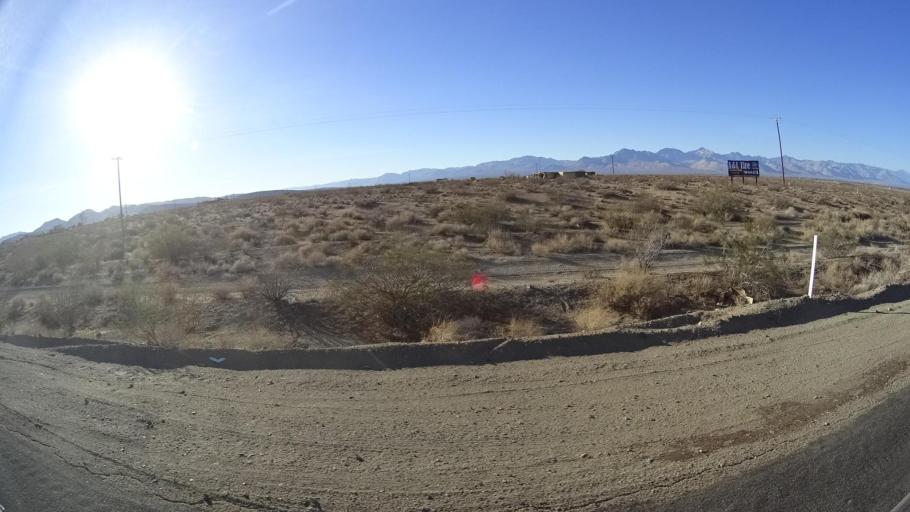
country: US
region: California
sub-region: Kern County
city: Ridgecrest
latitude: 35.5709
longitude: -117.7141
